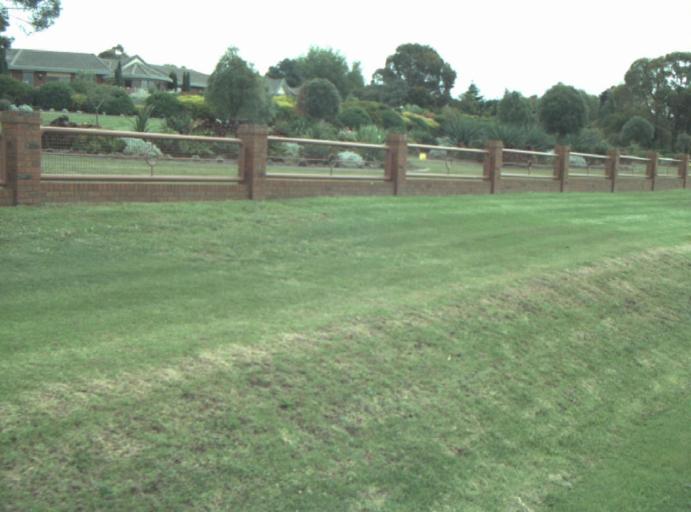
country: AU
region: Victoria
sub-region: Greater Geelong
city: Bell Post Hill
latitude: -38.0853
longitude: 144.3259
